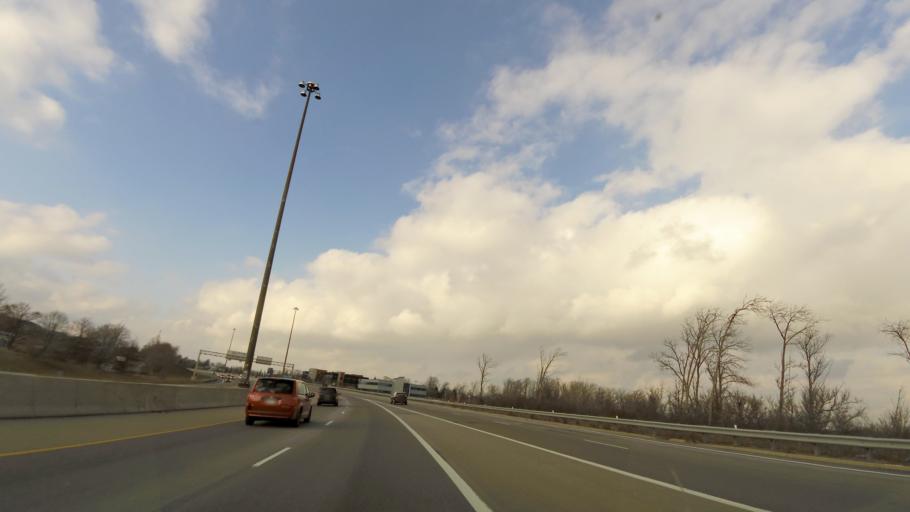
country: CA
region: Ontario
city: Waterloo
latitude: 43.4713
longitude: -80.4750
